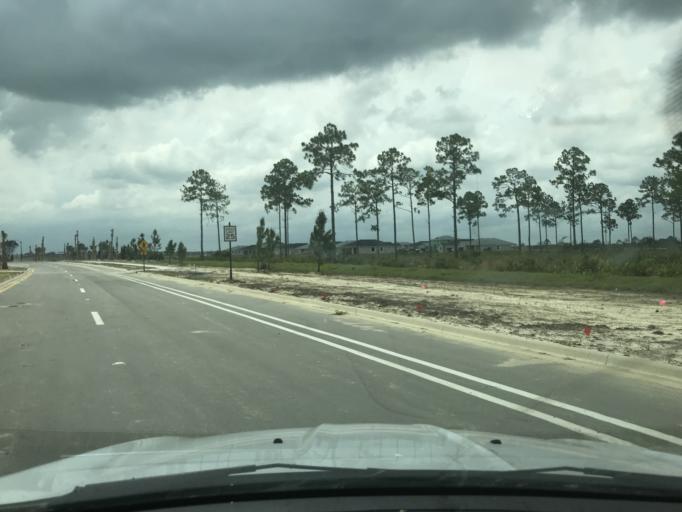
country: US
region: Florida
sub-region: Lee County
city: Olga
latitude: 26.7882
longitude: -81.7303
